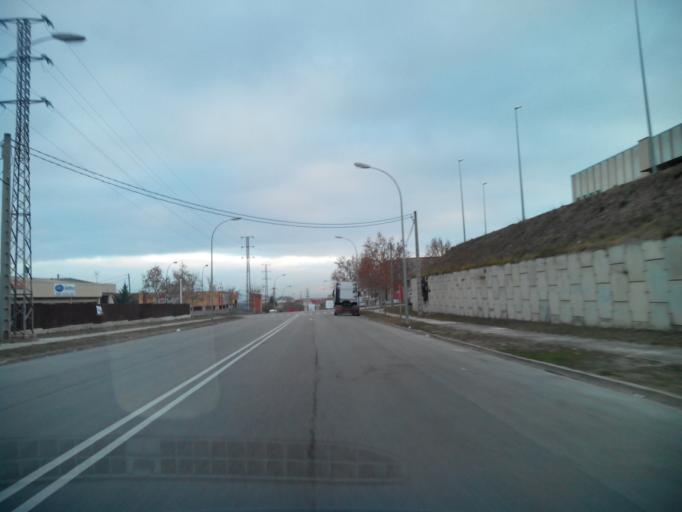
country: ES
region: Catalonia
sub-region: Provincia de Barcelona
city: Manresa
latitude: 41.7120
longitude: 1.8477
